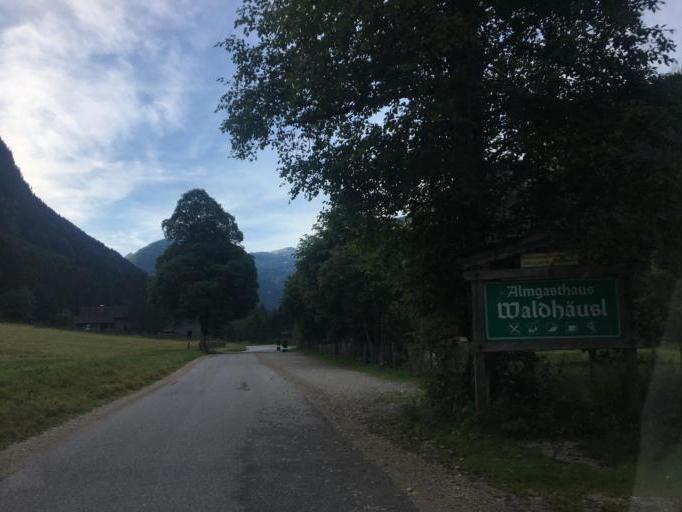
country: AT
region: Styria
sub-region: Politischer Bezirk Liezen
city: Schladming
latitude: 47.3478
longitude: 13.7271
